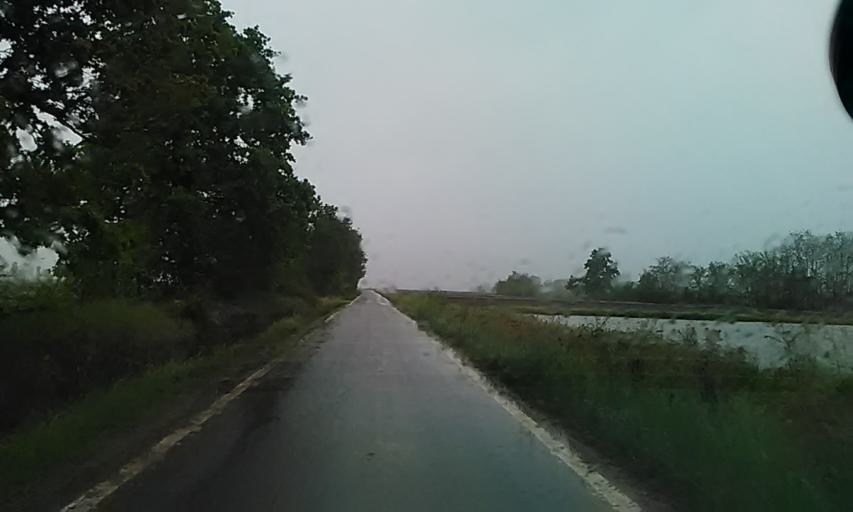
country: IT
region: Piedmont
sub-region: Provincia di Vercelli
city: San Giacomo Vercellese
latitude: 45.4859
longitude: 8.3367
